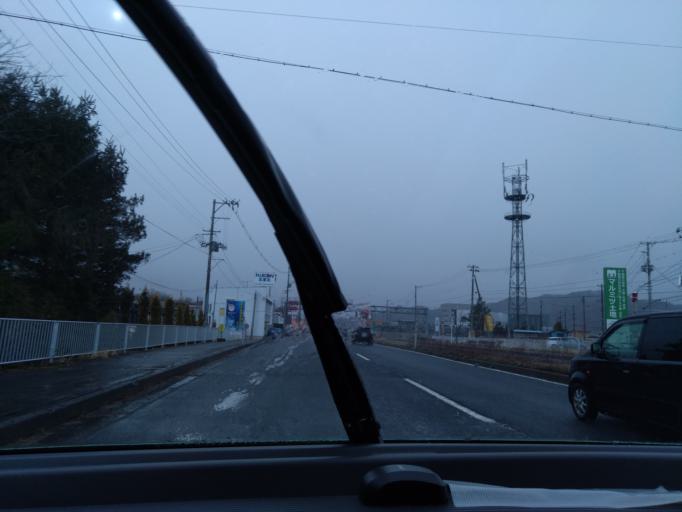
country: JP
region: Iwate
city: Morioka-shi
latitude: 39.7061
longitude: 141.0835
